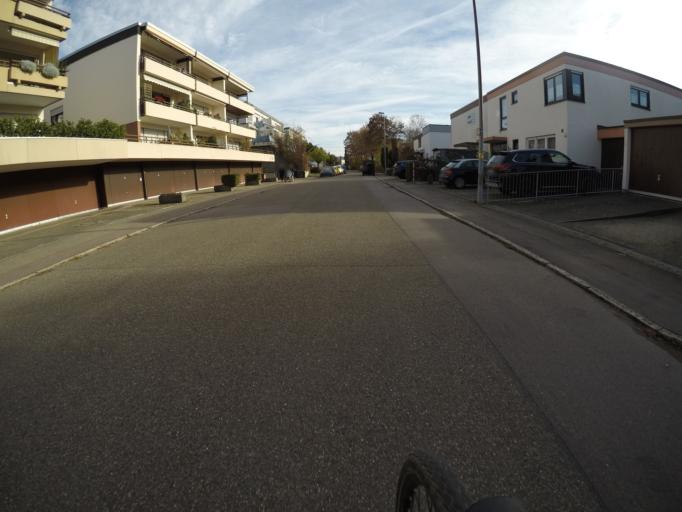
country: DE
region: Baden-Wuerttemberg
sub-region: Regierungsbezirk Stuttgart
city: Weinstadt-Endersbach
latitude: 48.8171
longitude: 9.3808
